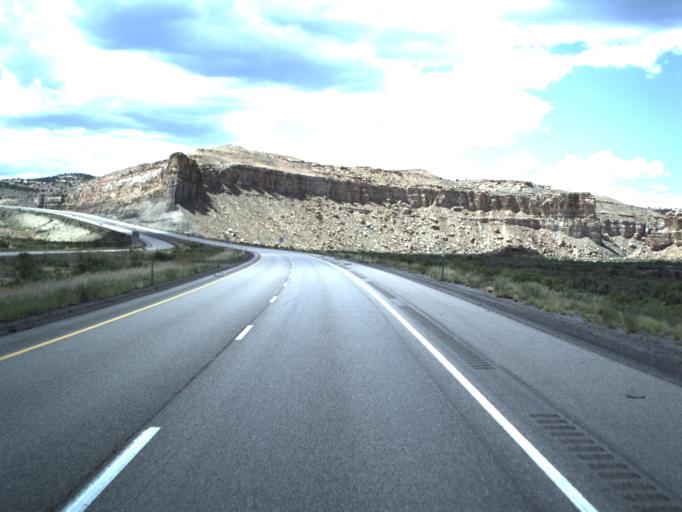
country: US
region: Utah
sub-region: Emery County
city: Ferron
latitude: 38.8101
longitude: -111.2508
